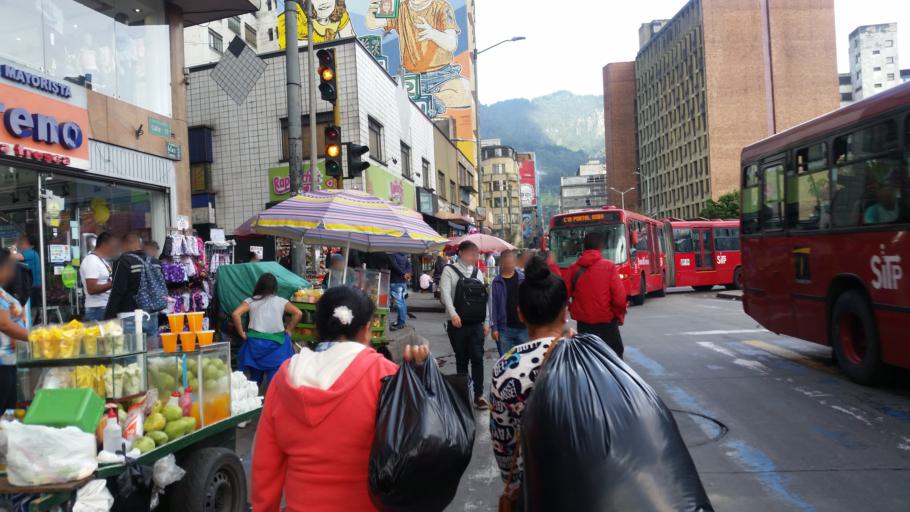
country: CO
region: Bogota D.C.
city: Bogota
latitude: 4.6027
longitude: -74.0783
